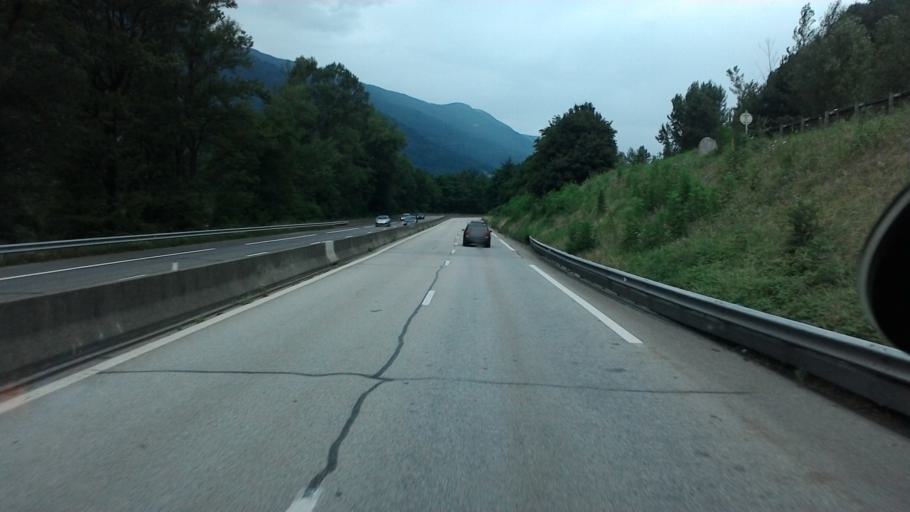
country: FR
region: Rhone-Alpes
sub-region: Departement de la Savoie
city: La Bathie
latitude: 45.5742
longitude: 6.4627
